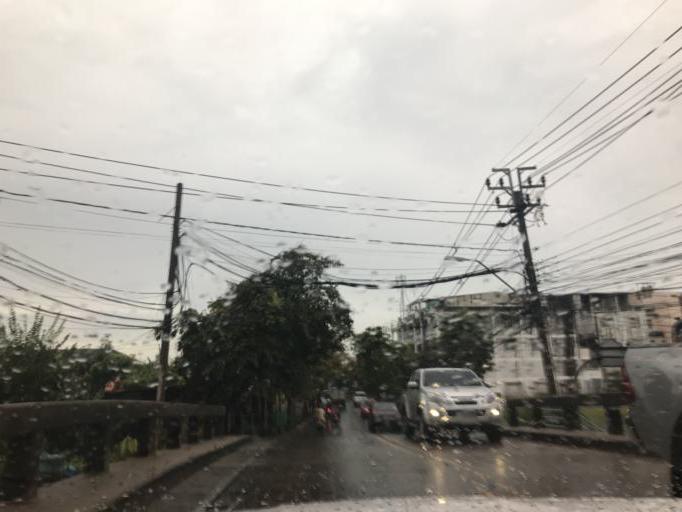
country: TH
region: Bangkok
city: Phasi Charoen
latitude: 13.7339
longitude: 100.4340
